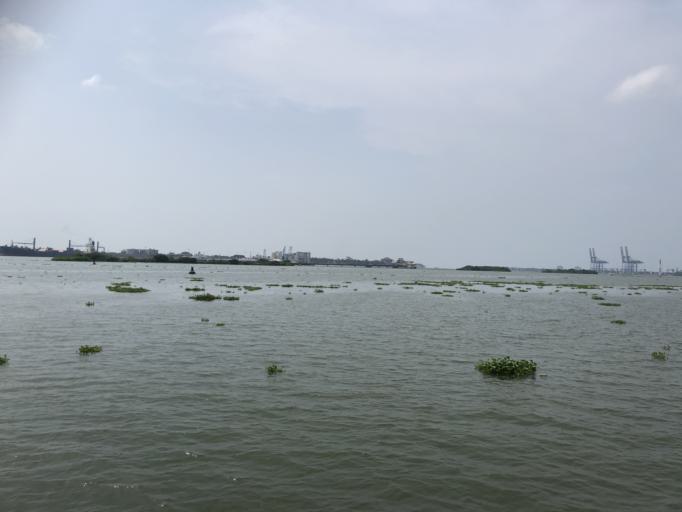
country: IN
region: Kerala
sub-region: Ernakulam
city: Cochin
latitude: 9.9749
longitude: 76.2766
